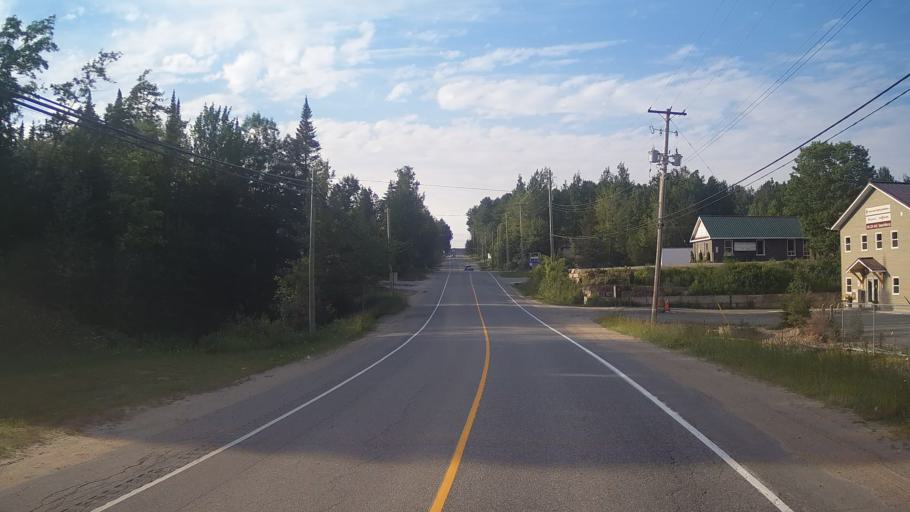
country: CA
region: Ontario
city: Huntsville
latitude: 45.3512
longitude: -79.2016
